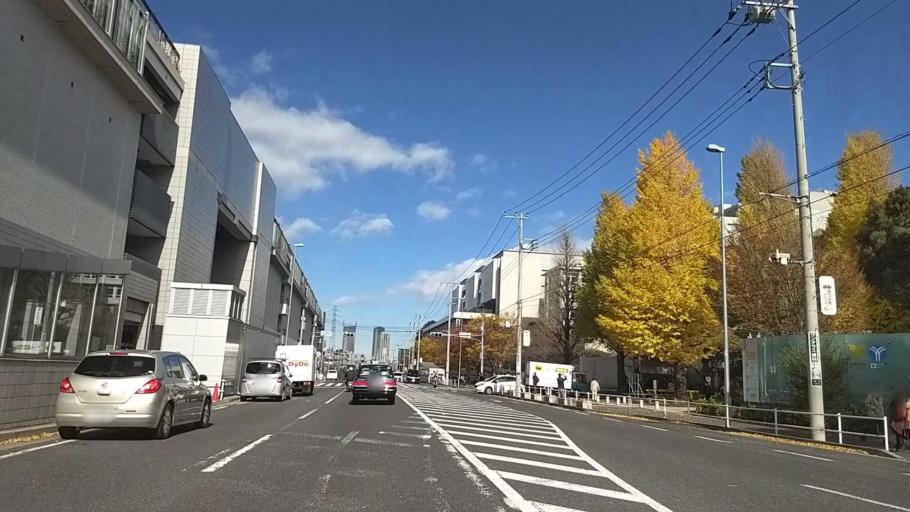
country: JP
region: Kanagawa
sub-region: Kawasaki-shi
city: Kawasaki
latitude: 35.5527
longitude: 139.6470
